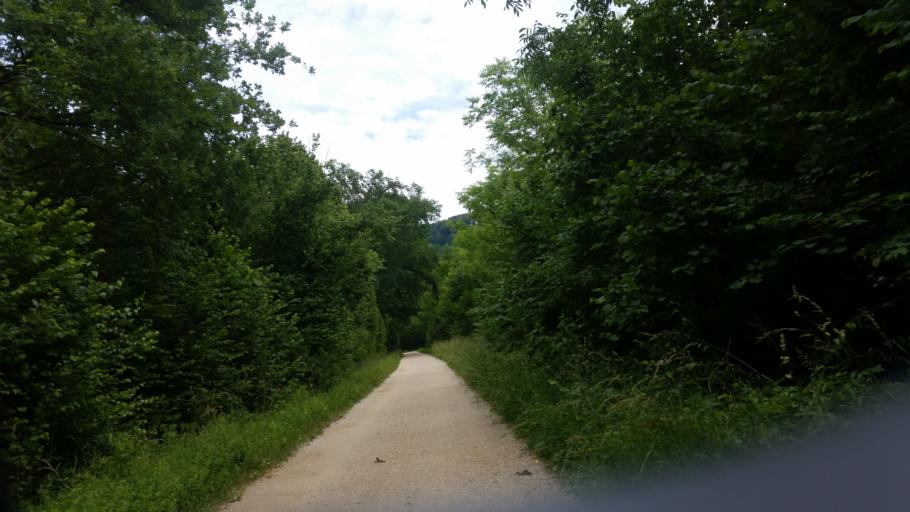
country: CH
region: Vaud
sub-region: Jura-Nord vaudois District
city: Yvonand
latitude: 46.7996
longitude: 6.7556
